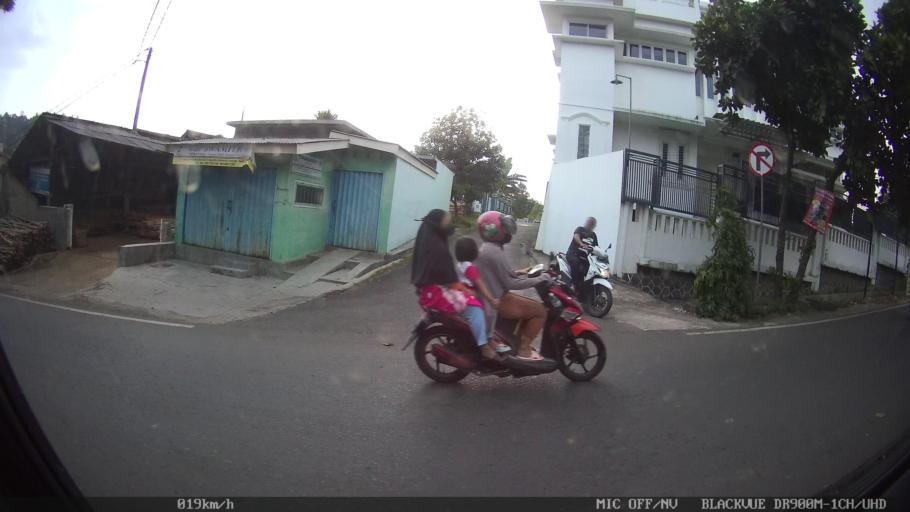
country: ID
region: Lampung
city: Kedaton
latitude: -5.4006
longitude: 105.2111
